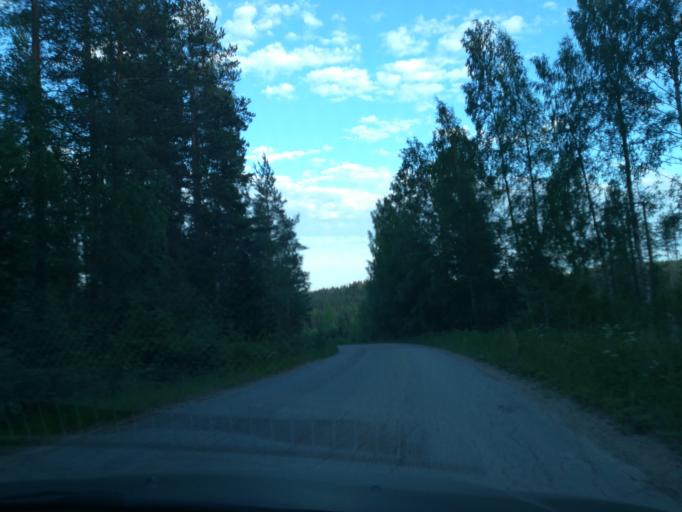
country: FI
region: Southern Savonia
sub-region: Mikkeli
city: Puumala
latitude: 61.5820
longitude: 28.1243
